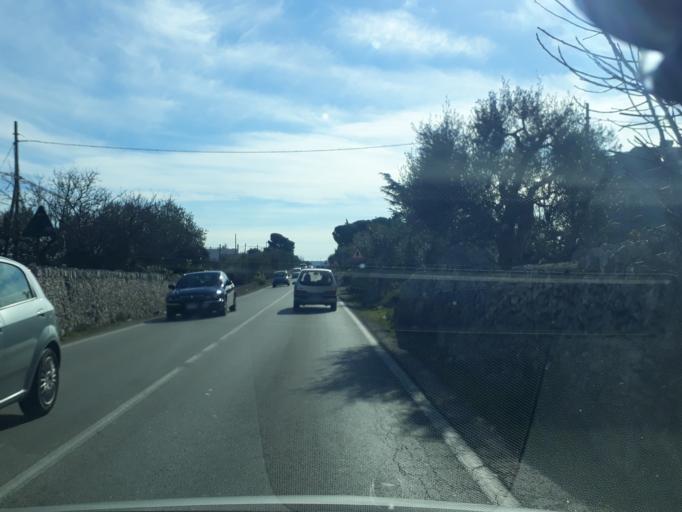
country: IT
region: Apulia
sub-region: Provincia di Bari
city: Locorotondo
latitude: 40.7450
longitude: 17.3312
